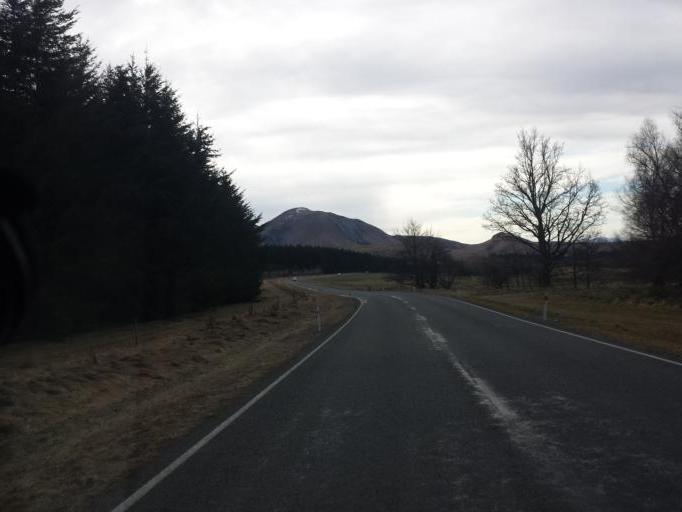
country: NZ
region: Canterbury
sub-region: Timaru District
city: Pleasant Point
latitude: -44.0433
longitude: 170.6848
